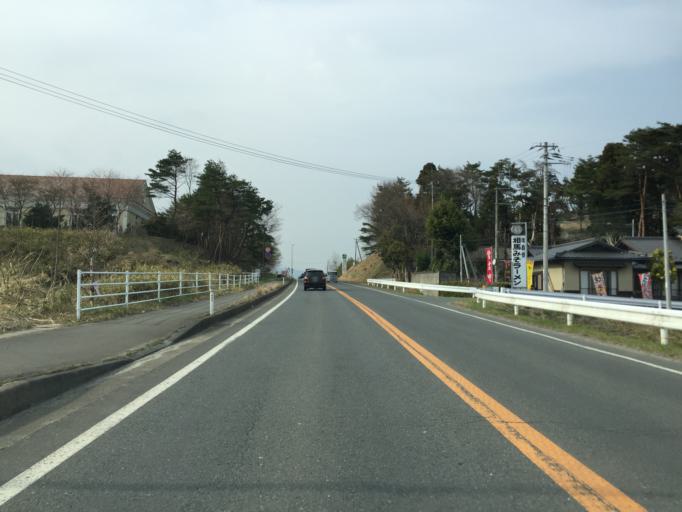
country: JP
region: Miyagi
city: Marumori
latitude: 37.7820
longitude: 140.9362
